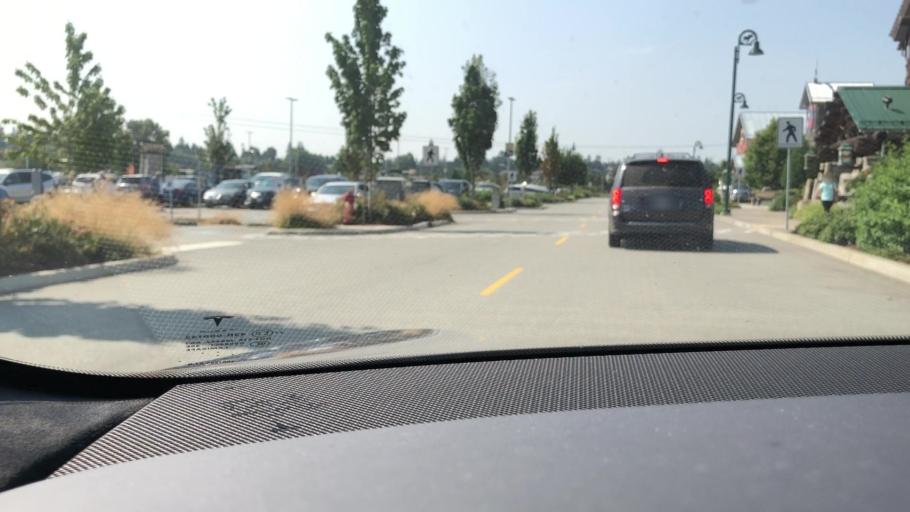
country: CA
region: British Columbia
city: Ladner
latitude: 49.0396
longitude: -123.0811
